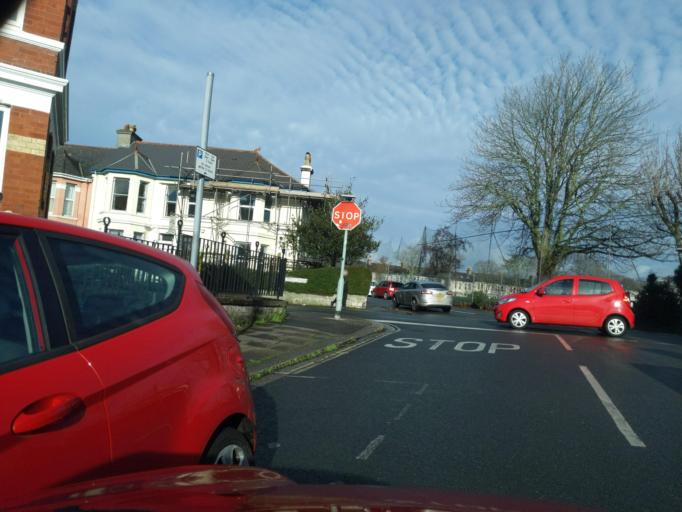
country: GB
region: England
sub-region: Plymouth
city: Plymouth
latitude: 50.3829
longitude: -4.1390
